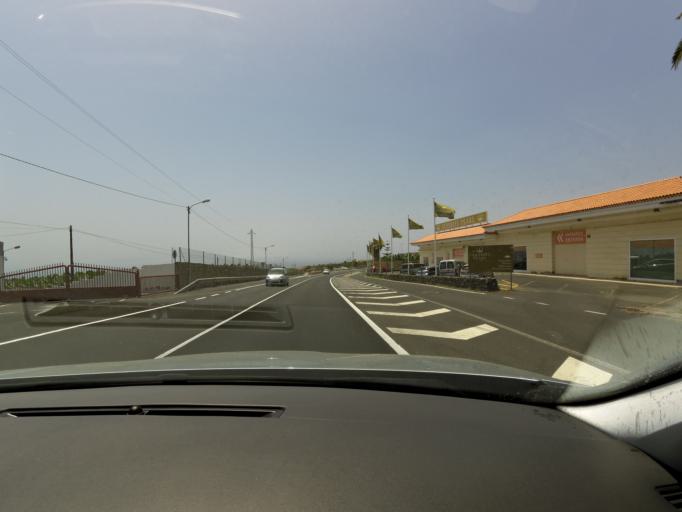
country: ES
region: Canary Islands
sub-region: Provincia de Santa Cruz de Tenerife
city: Adeje
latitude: 28.1287
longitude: -16.7591
